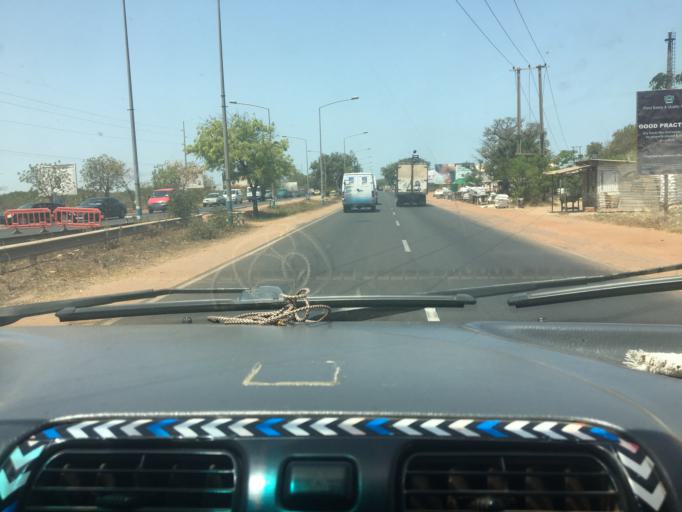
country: GM
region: Banjul
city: Bakau
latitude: 13.4683
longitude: -16.6309
